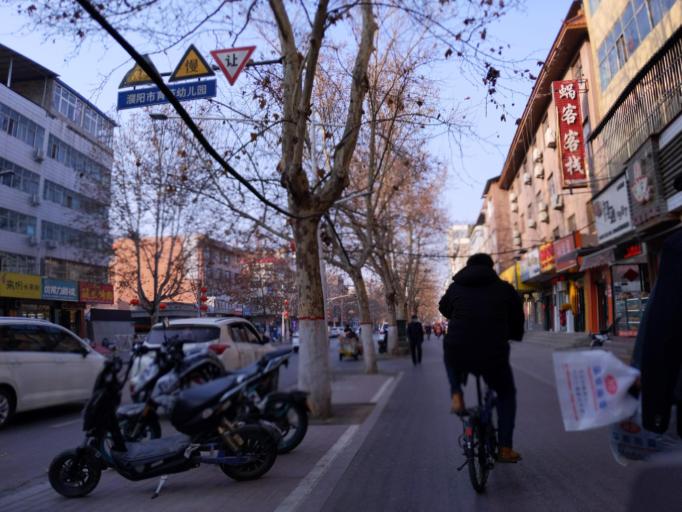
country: CN
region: Henan Sheng
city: Puyang
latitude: 35.7670
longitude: 115.0325
